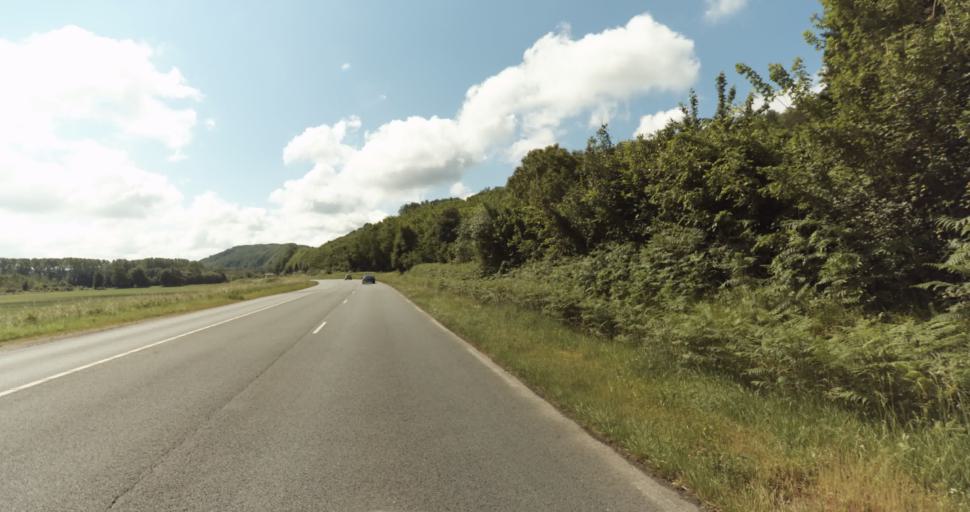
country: FR
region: Aquitaine
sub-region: Departement de la Dordogne
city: Belves
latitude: 44.8319
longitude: 0.9410
